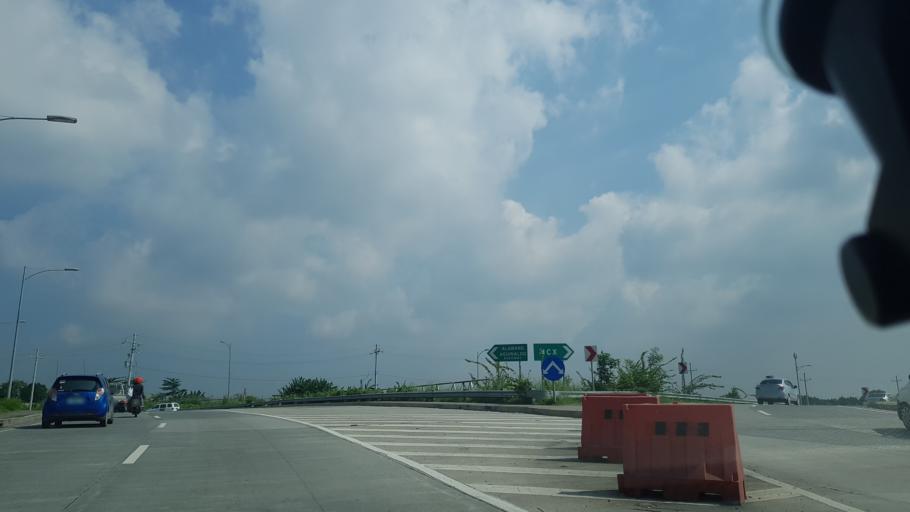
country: PH
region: Calabarzon
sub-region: Province of Laguna
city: San Pedro
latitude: 14.3749
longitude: 121.0141
